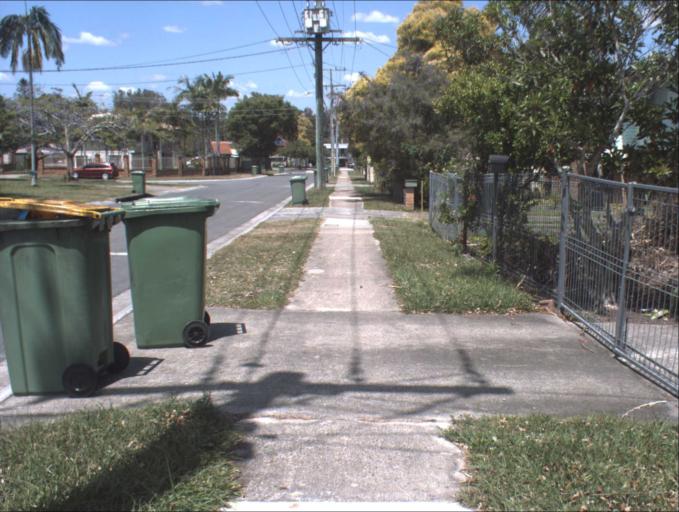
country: AU
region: Queensland
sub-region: Logan
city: Logan City
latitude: -27.6505
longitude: 153.1009
